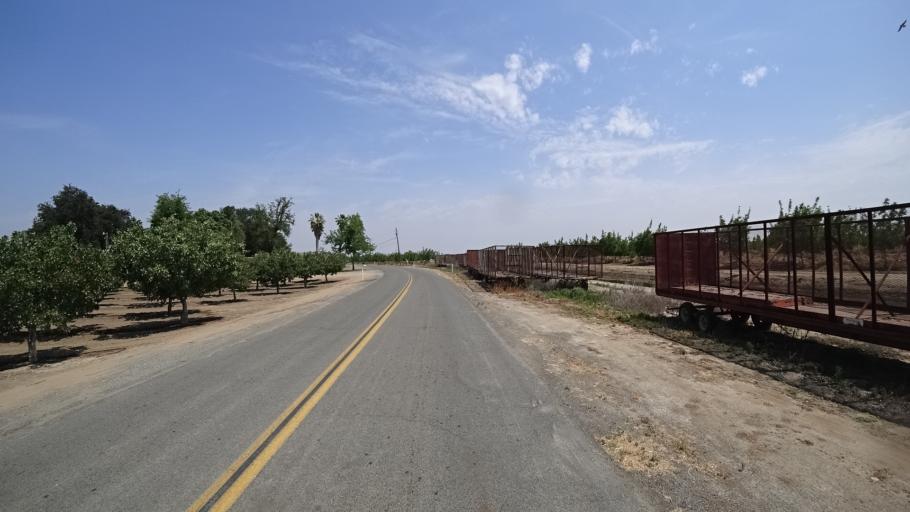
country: US
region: California
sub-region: Kings County
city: Lemoore
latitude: 36.3285
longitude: -119.7631
